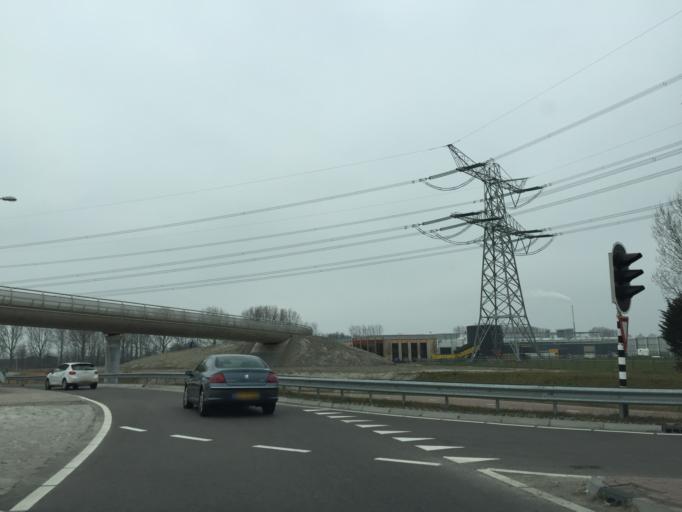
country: NL
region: South Holland
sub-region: Gemeente Westland
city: Naaldwijk
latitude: 51.9815
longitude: 4.2194
